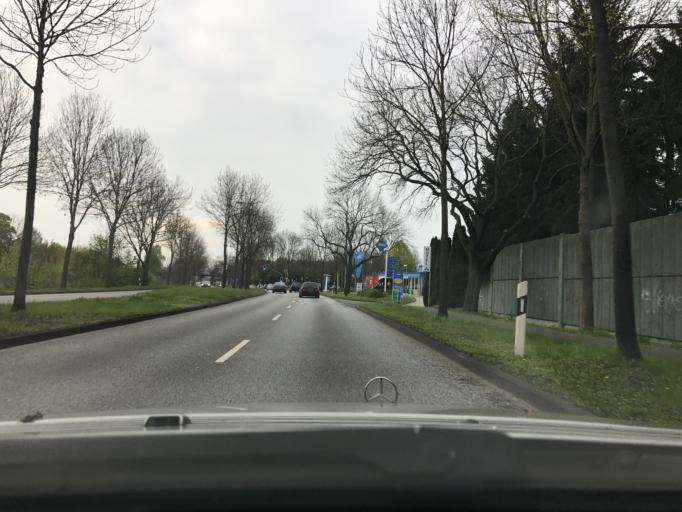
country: DE
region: Hesse
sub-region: Regierungsbezirk Kassel
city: Kassel
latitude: 51.2939
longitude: 9.5107
